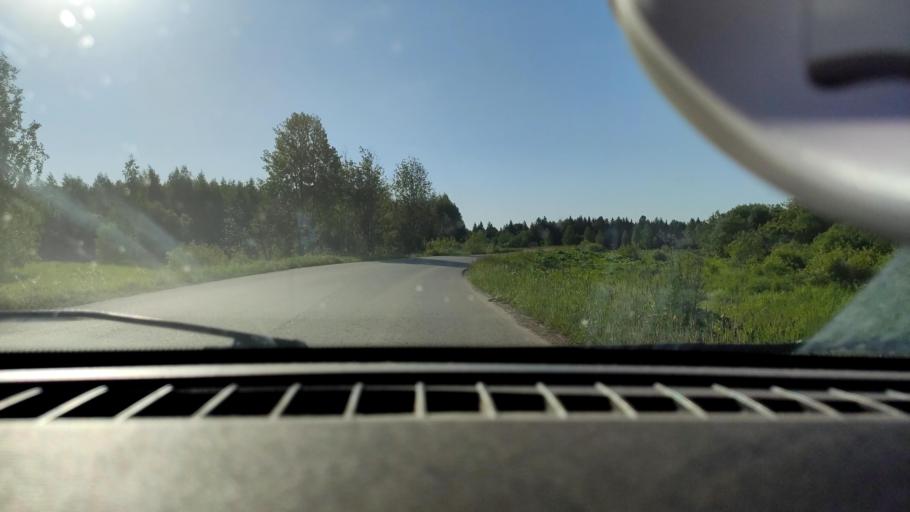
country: RU
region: Perm
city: Polazna
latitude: 58.2159
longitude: 56.4202
